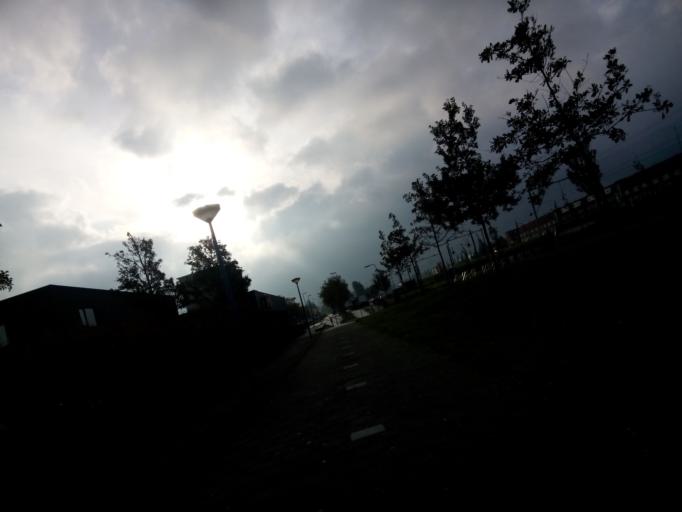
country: NL
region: South Holland
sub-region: Gemeente Maassluis
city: Maassluis
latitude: 51.9239
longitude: 4.2398
